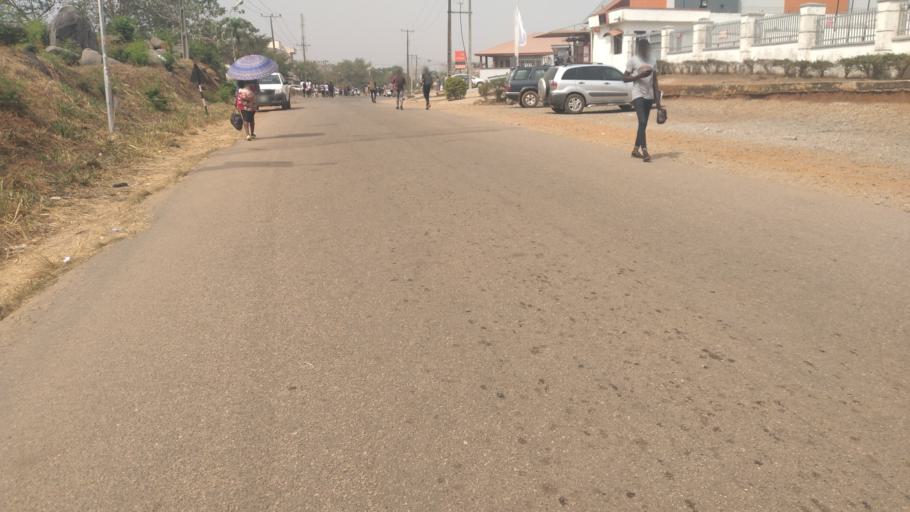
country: NG
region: Ondo
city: Ilare
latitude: 7.3005
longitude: 5.1394
